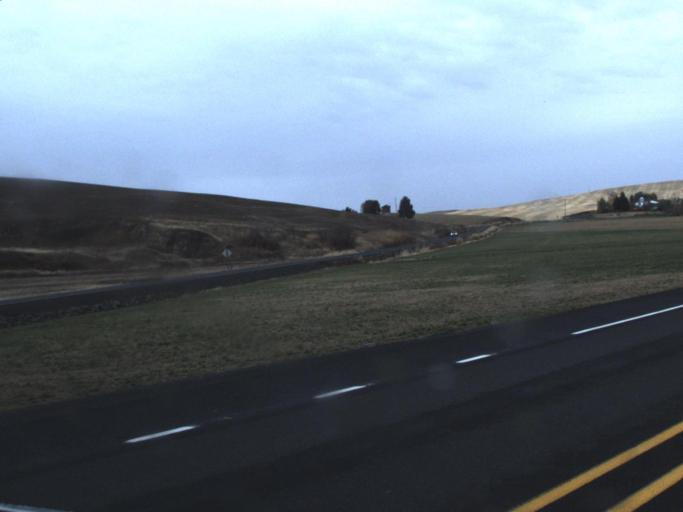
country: US
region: Washington
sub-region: Whitman County
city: Pullman
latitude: 46.5722
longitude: -117.1454
